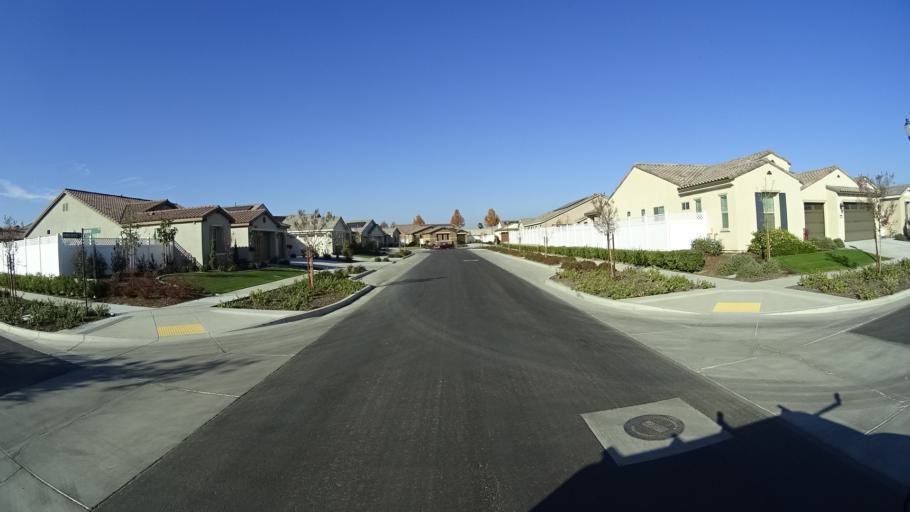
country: US
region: California
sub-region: Kern County
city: Rosedale
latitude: 35.3382
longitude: -119.1554
